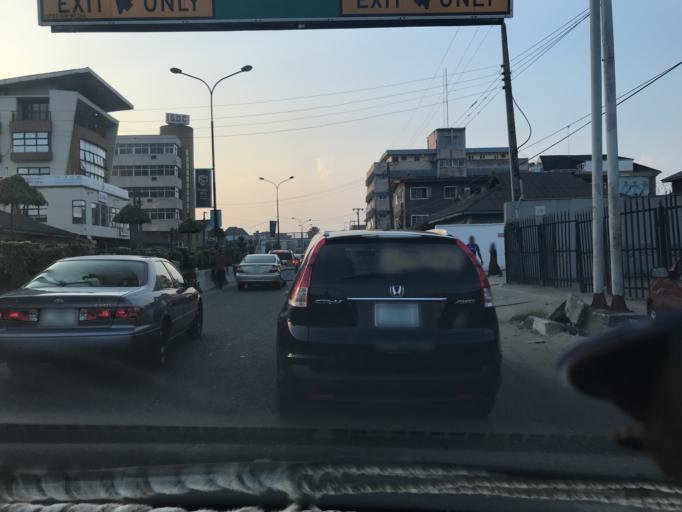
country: NG
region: Lagos
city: Makoko
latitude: 6.4932
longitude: 3.3815
